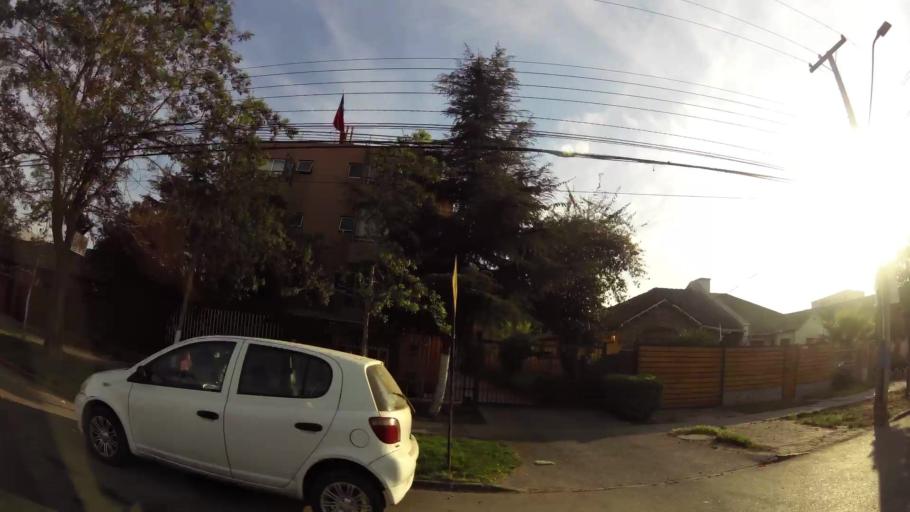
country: CL
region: Santiago Metropolitan
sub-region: Provincia de Santiago
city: La Pintana
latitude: -33.5330
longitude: -70.6707
